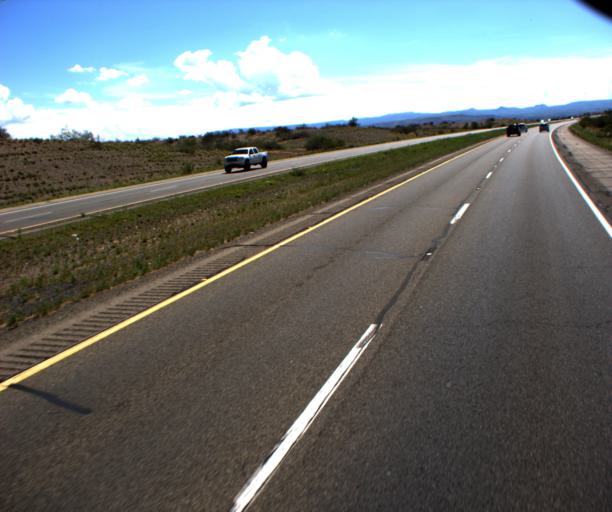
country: US
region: Arizona
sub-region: Yavapai County
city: Spring Valley
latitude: 34.3476
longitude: -112.1480
